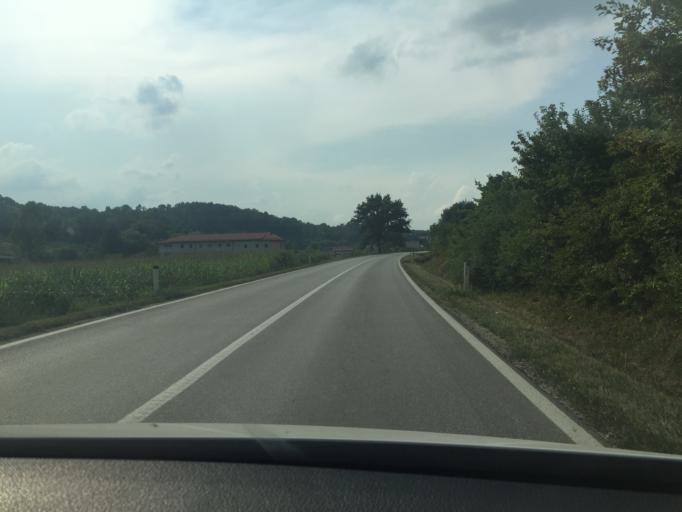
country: BA
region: Federation of Bosnia and Herzegovina
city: Mionica
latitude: 44.8213
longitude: 18.4601
